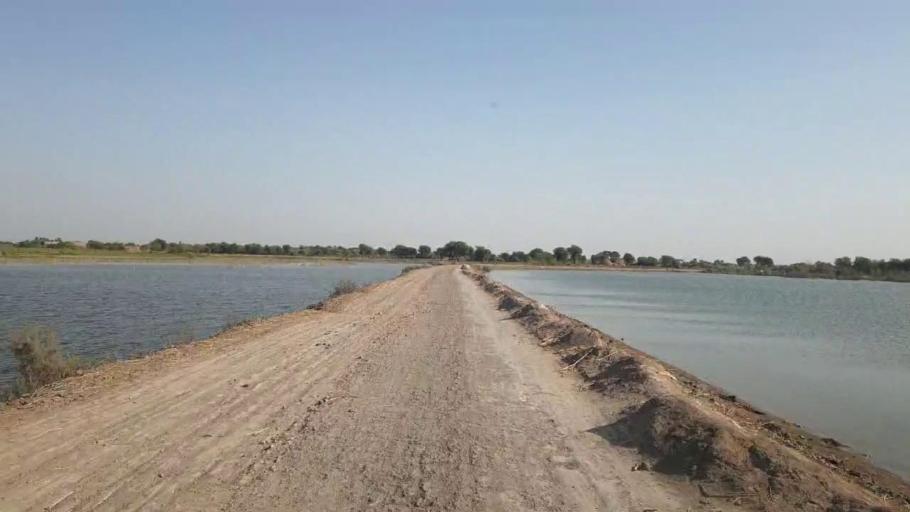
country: PK
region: Sindh
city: Matli
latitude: 25.0073
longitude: 68.7427
